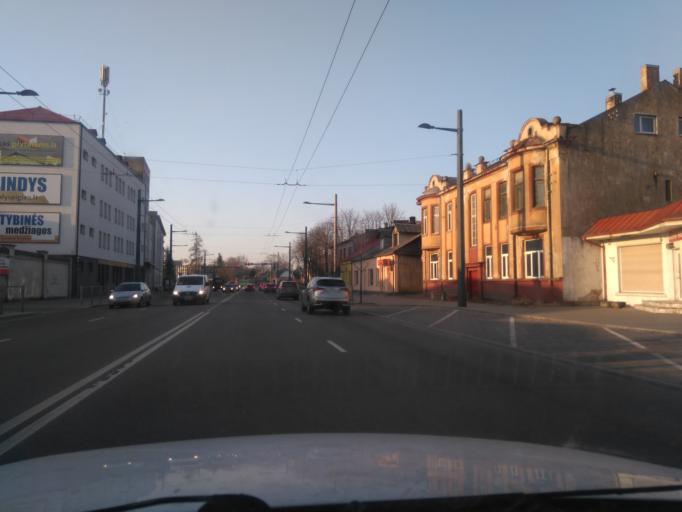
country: LT
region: Kauno apskritis
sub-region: Kaunas
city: Aleksotas
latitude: 54.8748
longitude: 23.9360
